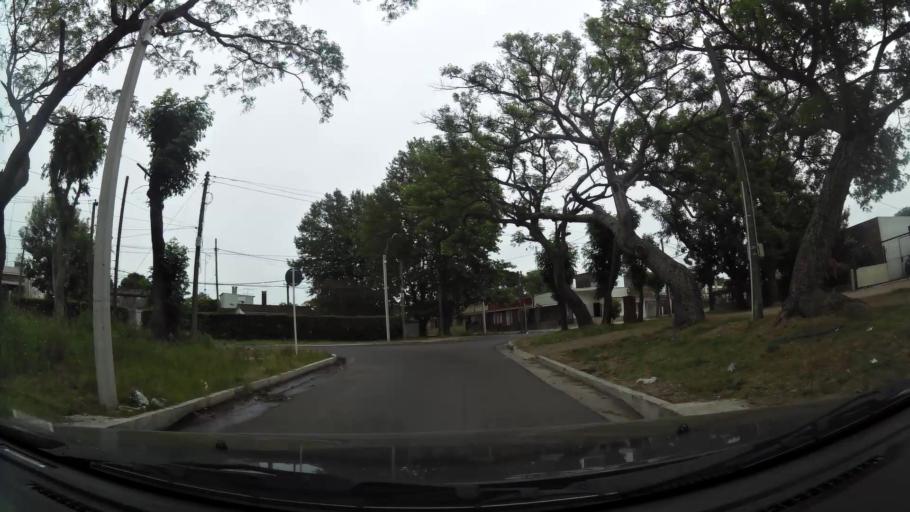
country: UY
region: Canelones
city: Las Piedras
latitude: -34.7299
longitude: -56.2123
